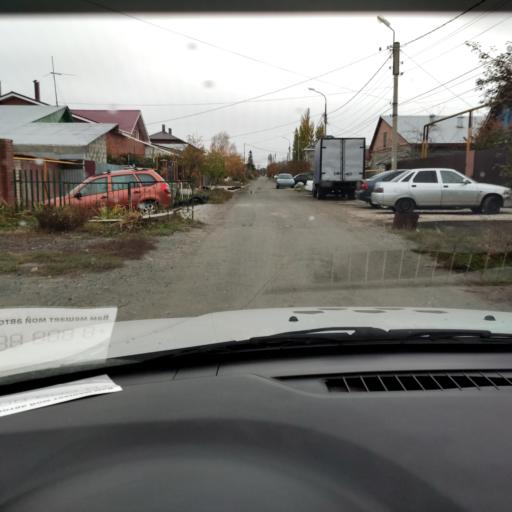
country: RU
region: Samara
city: Tol'yatti
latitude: 53.5378
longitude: 49.4203
